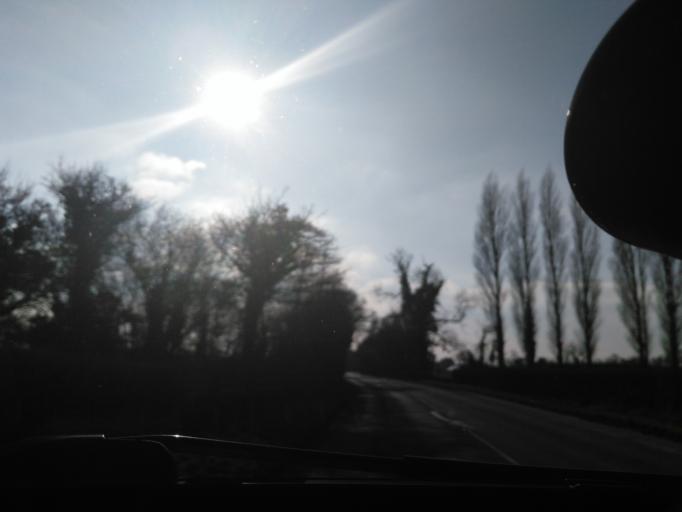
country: GB
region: England
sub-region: Wiltshire
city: Malmesbury
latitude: 51.5460
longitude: -2.1213
